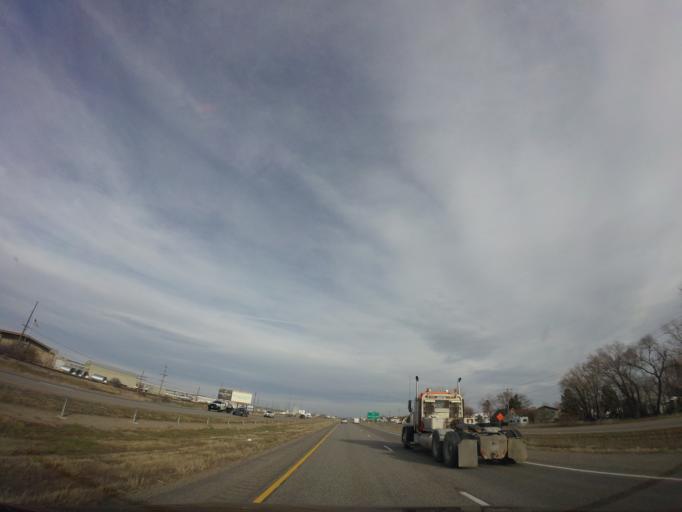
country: US
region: Montana
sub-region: Yellowstone County
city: Billings
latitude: 45.7398
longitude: -108.5881
